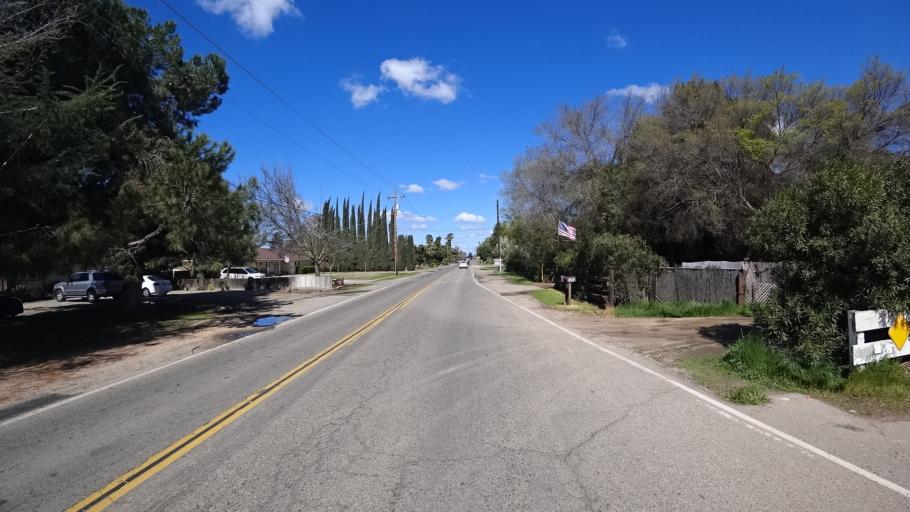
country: US
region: California
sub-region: Fresno County
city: West Park
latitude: 36.7908
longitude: -119.8894
